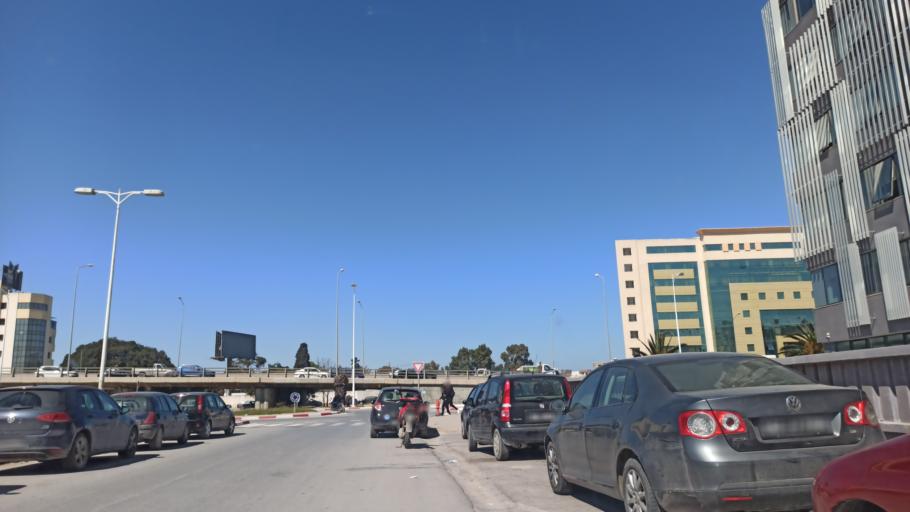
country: TN
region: Ariana
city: Ariana
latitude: 36.8503
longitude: 10.1970
